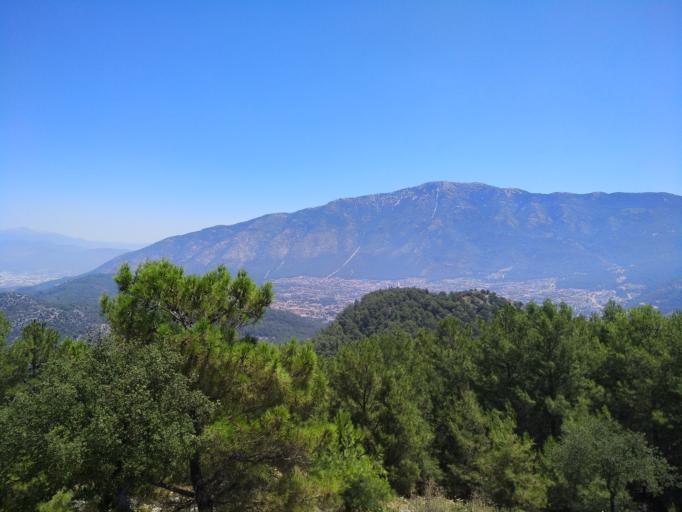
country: TR
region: Mugla
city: OEluedeniz
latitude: 36.5679
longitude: 29.1074
